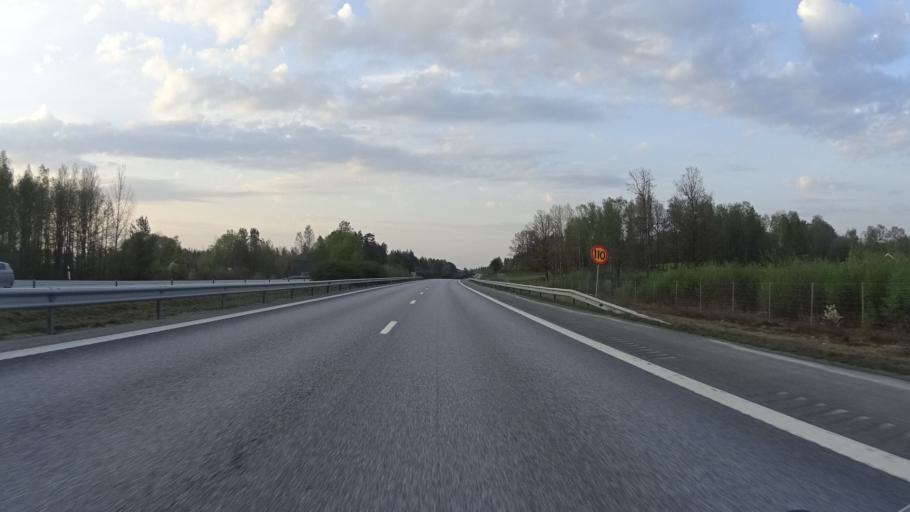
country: SE
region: Joenkoeping
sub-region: Varnamo Kommun
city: Varnamo
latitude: 57.1680
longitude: 14.0729
